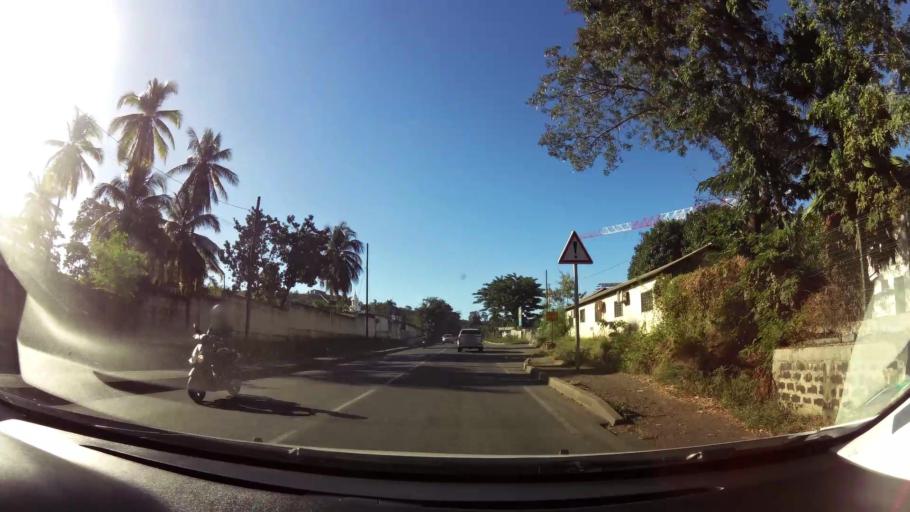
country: YT
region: Mamoudzou
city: Mamoudzou
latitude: -12.7656
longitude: 45.2252
